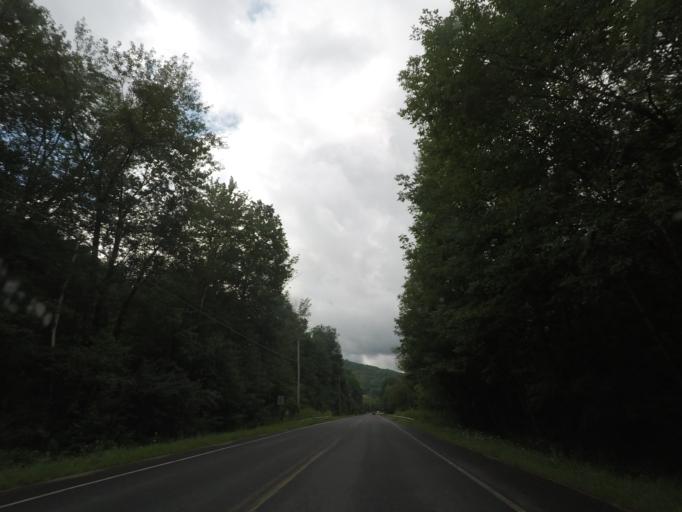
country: US
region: Massachusetts
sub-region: Berkshire County
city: Lanesborough
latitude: 42.5628
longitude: -73.2866
